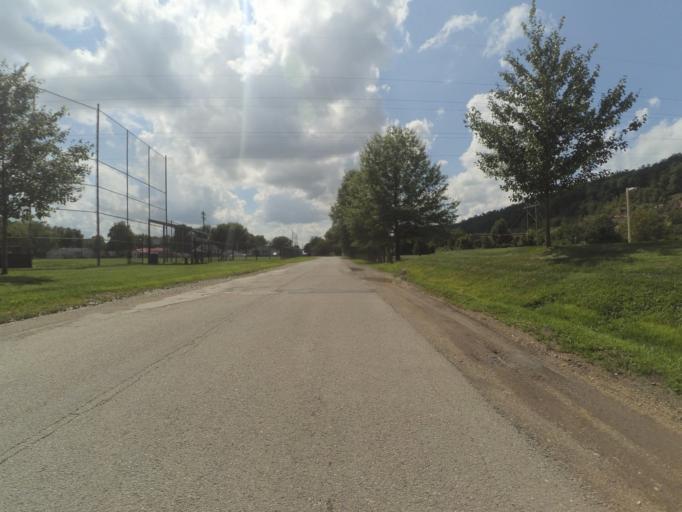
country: US
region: West Virginia
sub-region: Cabell County
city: Pea Ridge
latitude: 38.4178
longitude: -82.3557
